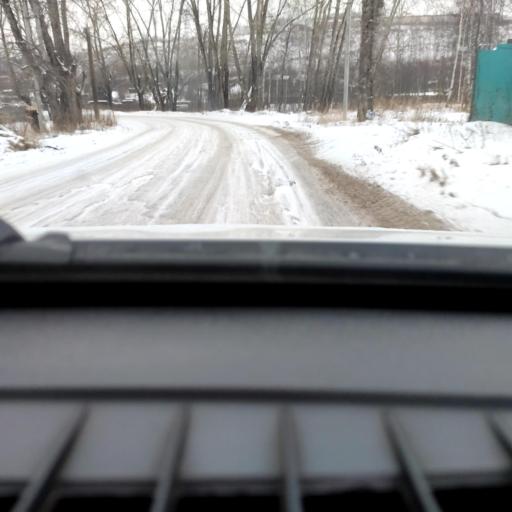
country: RU
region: Perm
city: Perm
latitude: 58.1037
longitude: 56.3660
